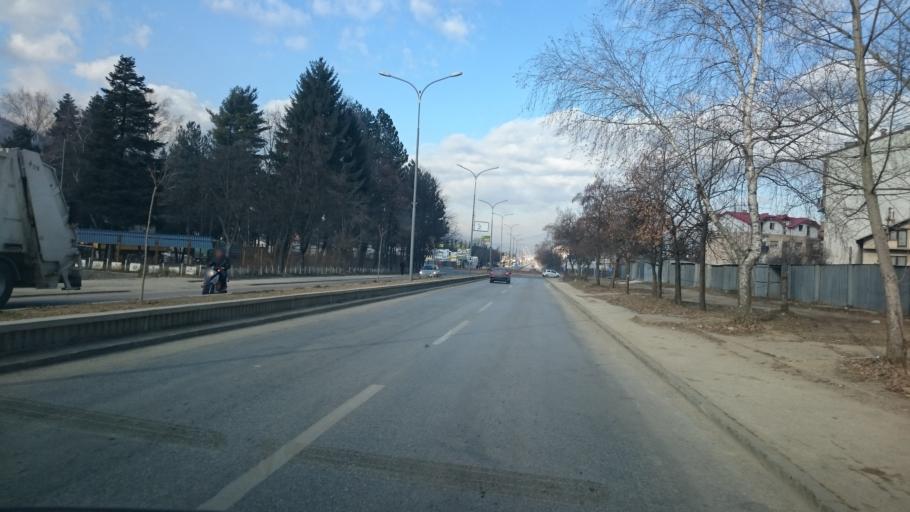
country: MK
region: Kicevo
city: Kicevo
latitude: 41.5052
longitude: 20.9525
